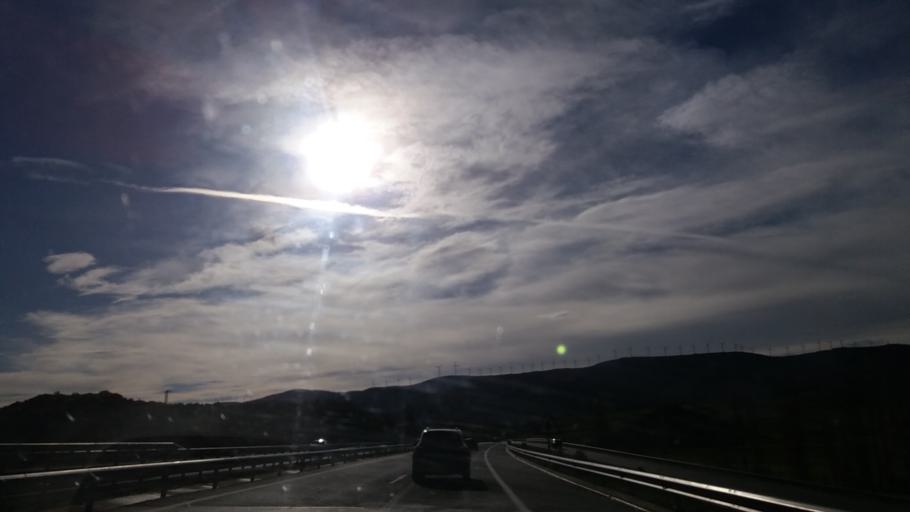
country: ES
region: Navarre
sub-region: Provincia de Navarra
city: Monreal
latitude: 42.6926
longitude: -1.4798
